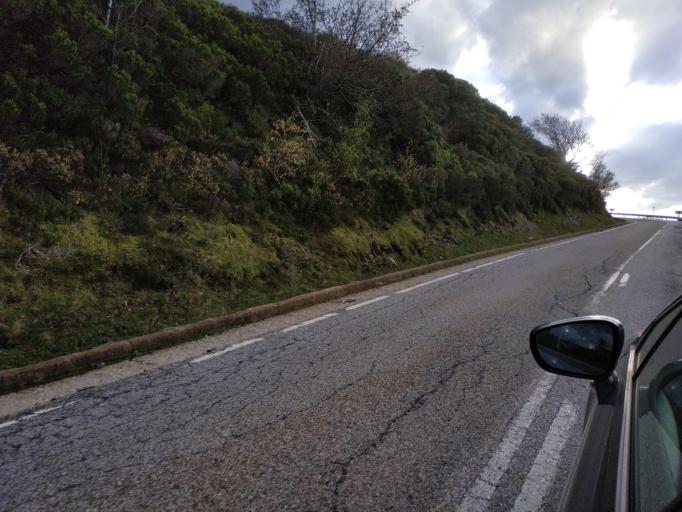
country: ES
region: Castille and Leon
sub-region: Provincia de Leon
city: Candin
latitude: 42.8683
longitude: -6.8229
